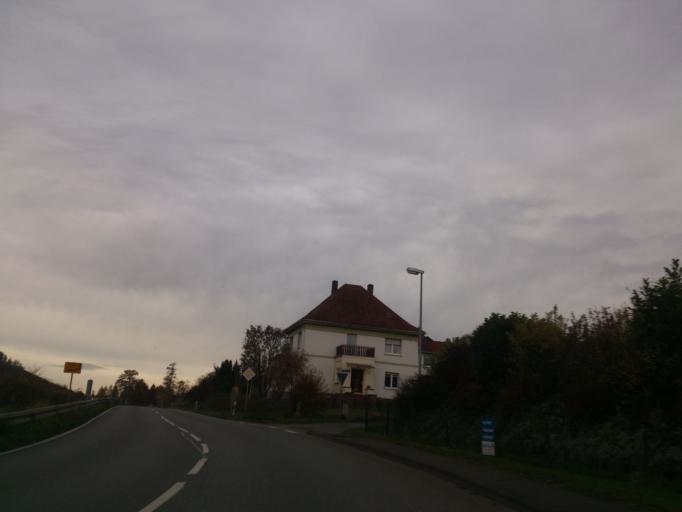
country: DE
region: North Rhine-Westphalia
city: Beverungen
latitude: 51.7116
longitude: 9.2910
